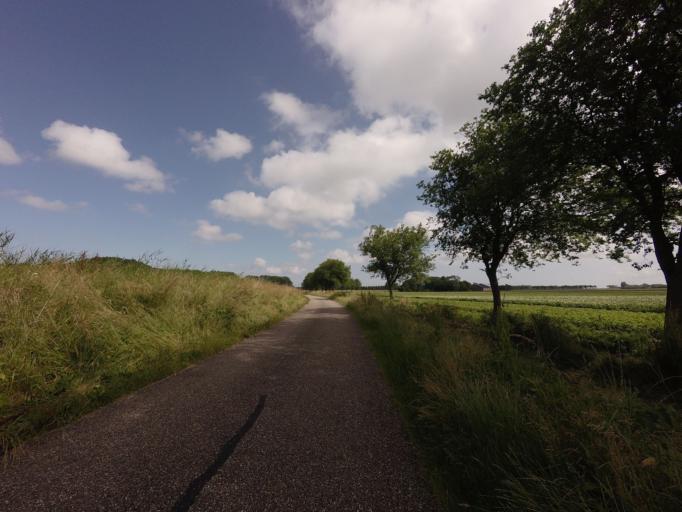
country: NL
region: North Holland
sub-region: Gemeente Schagen
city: Schagen
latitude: 52.8472
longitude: 4.8110
